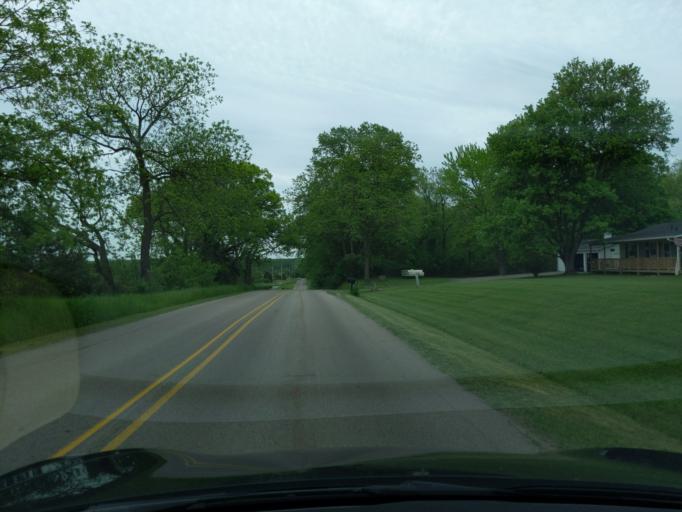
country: US
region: Michigan
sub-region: Ingham County
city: Leslie
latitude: 42.4021
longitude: -84.3359
